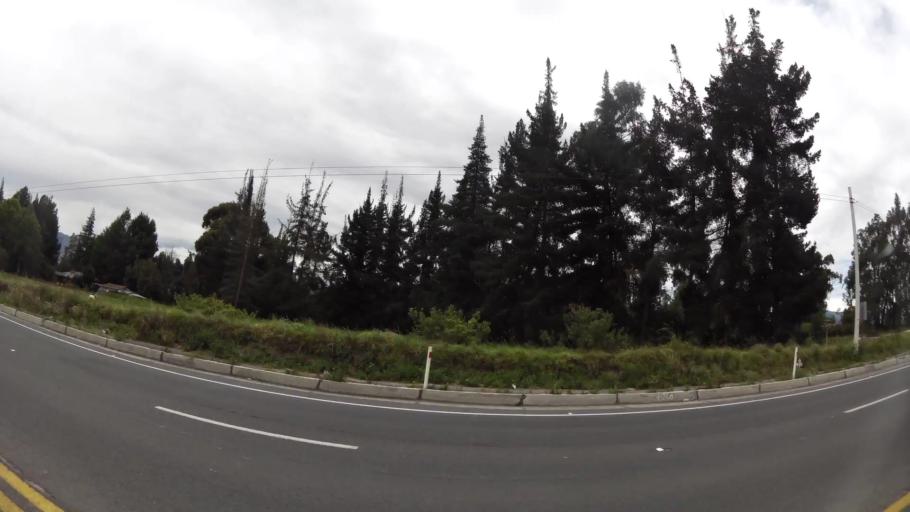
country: EC
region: Cotopaxi
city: San Miguel de Salcedo
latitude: -0.9972
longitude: -78.5944
